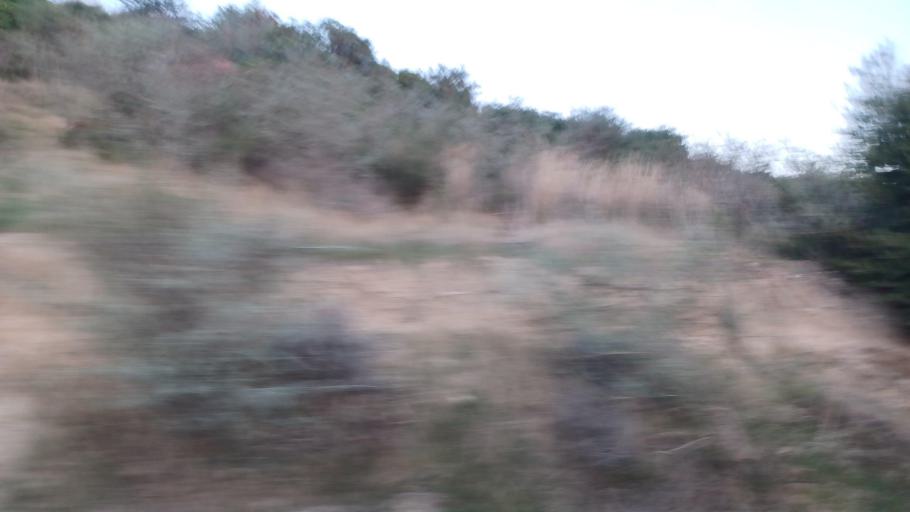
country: CY
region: Pafos
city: Polis
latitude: 34.9861
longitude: 32.4395
